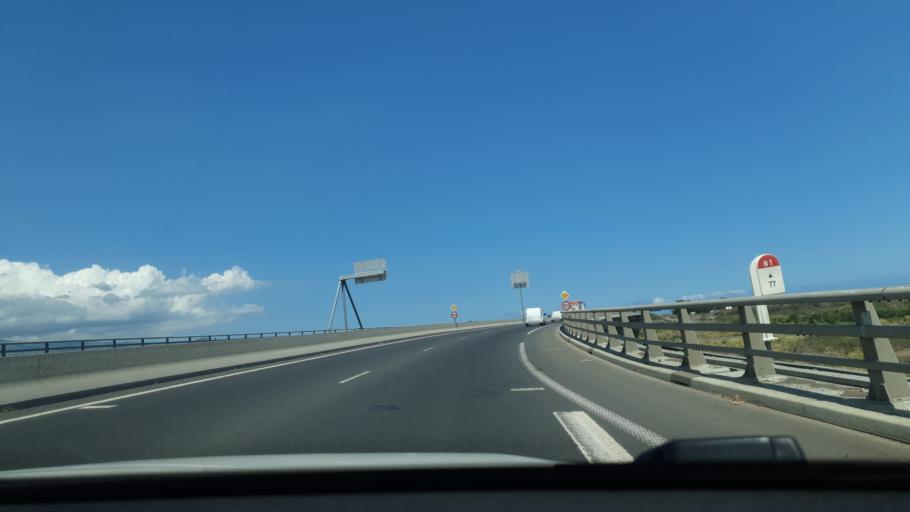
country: RE
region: Reunion
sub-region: Reunion
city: Saint-Louis
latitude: -21.2926
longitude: 55.4127
